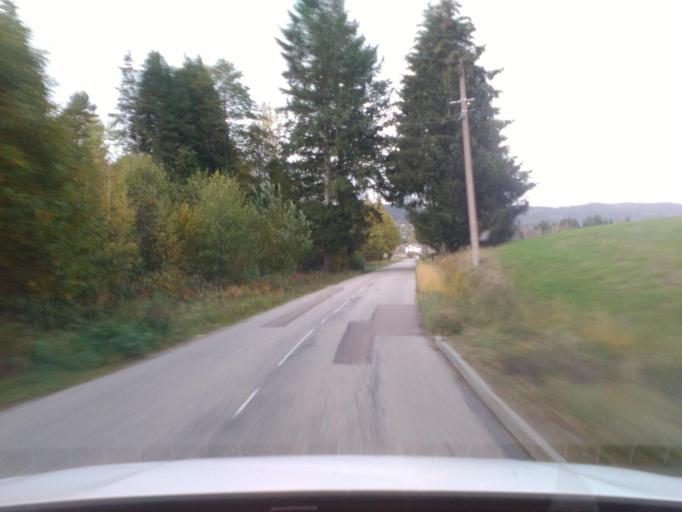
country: FR
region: Lorraine
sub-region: Departement des Vosges
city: Saint-Ame
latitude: 48.0369
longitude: 6.6720
